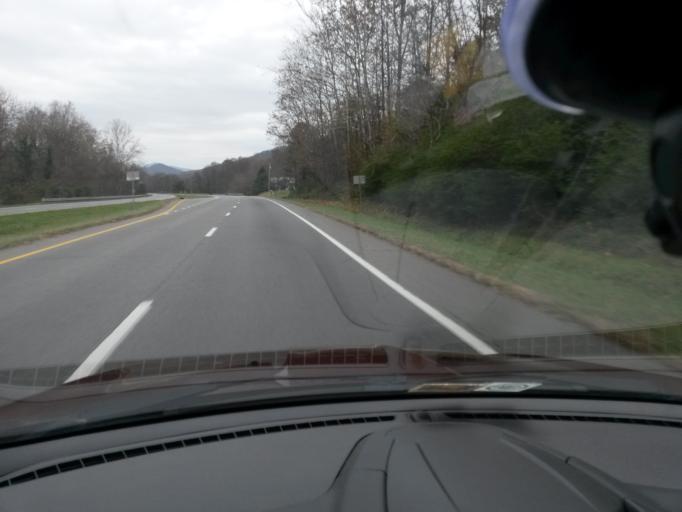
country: US
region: Virginia
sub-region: Nelson County
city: Nellysford
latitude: 37.8880
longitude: -78.7086
